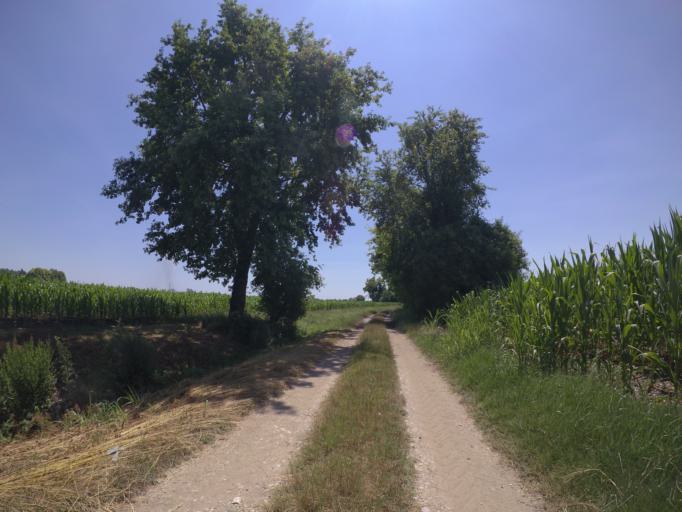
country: IT
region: Friuli Venezia Giulia
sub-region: Provincia di Udine
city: Talmassons
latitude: 45.9205
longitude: 13.0928
